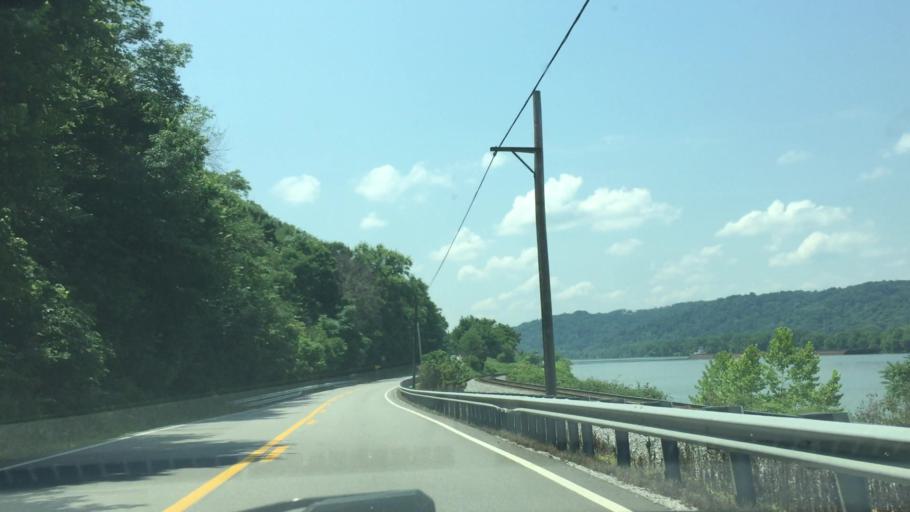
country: US
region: Ohio
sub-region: Belmont County
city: Powhatan Point
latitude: 39.7854
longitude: -80.8382
